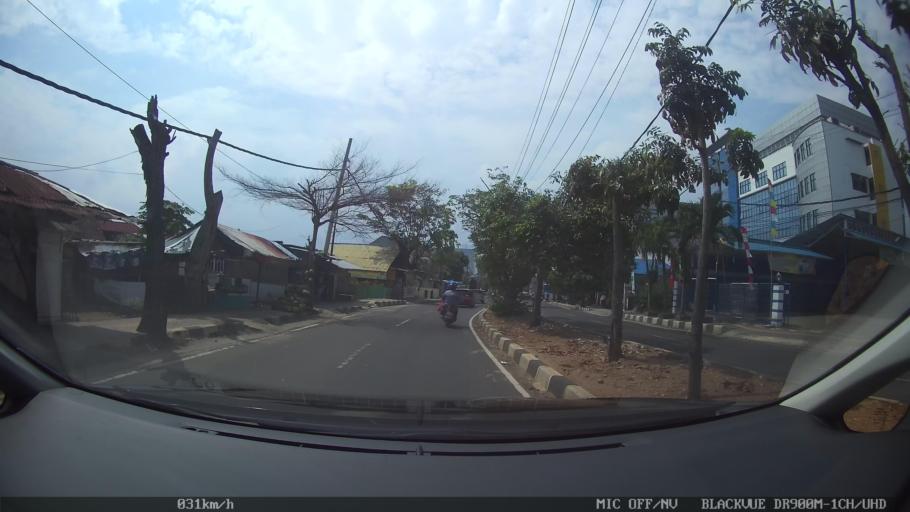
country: ID
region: Lampung
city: Bandarlampung
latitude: -5.4342
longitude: 105.2504
